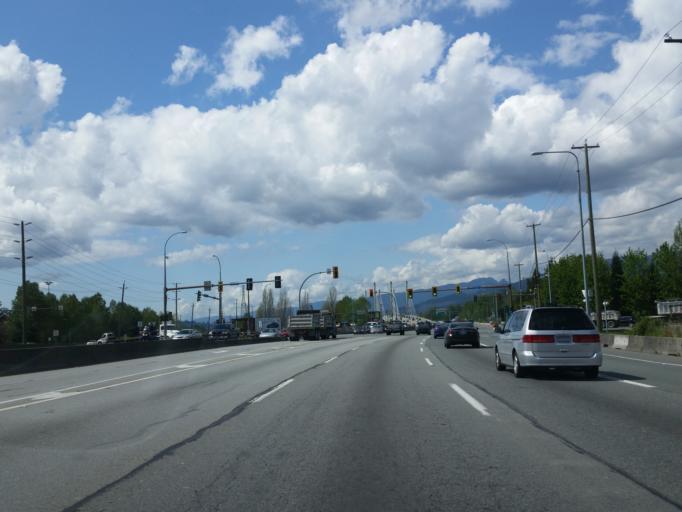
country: CA
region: British Columbia
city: Pitt Meadows
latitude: 49.2425
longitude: -122.7184
